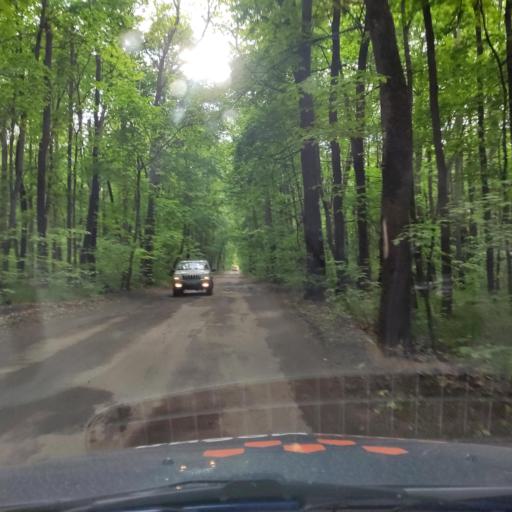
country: RU
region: Voronezj
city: Podgornoye
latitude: 51.7436
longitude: 39.2153
